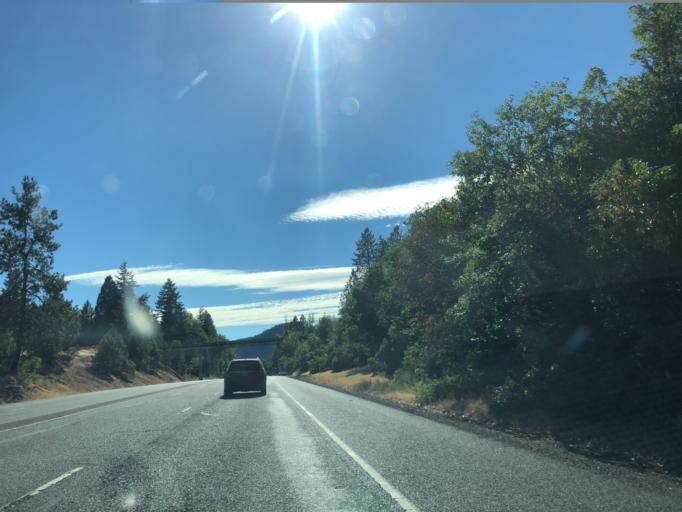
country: US
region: Oregon
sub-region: Josephine County
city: Redwood
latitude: 42.4117
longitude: -123.4192
